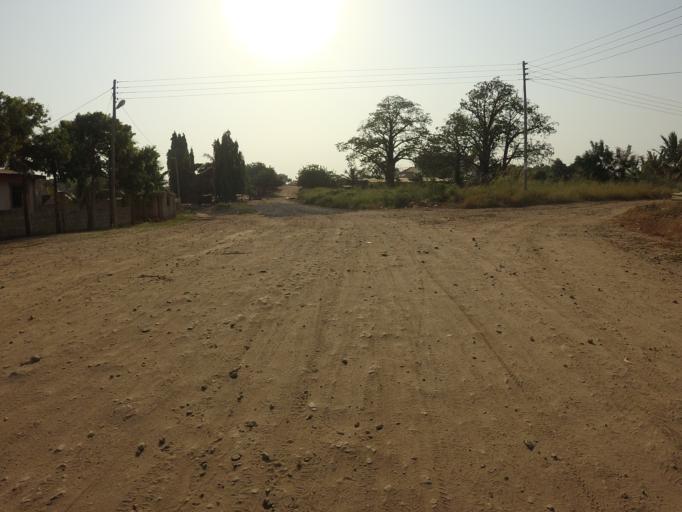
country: GH
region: Greater Accra
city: Tema
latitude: 5.7018
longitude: 0.0612
